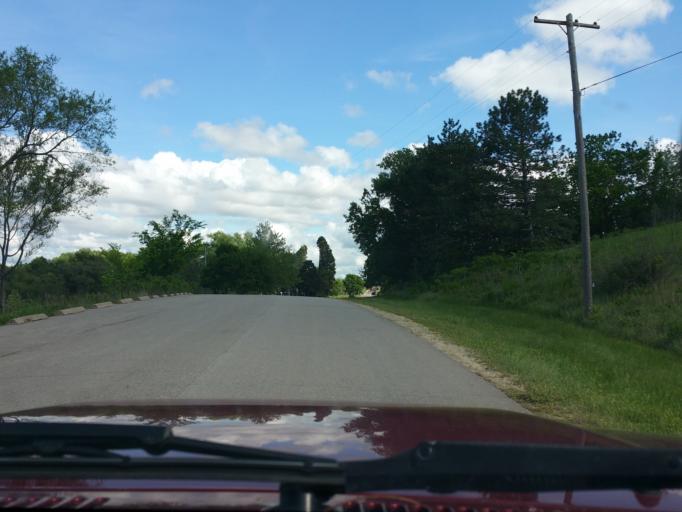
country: US
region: Kansas
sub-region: Riley County
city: Manhattan
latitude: 39.2499
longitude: -96.5996
